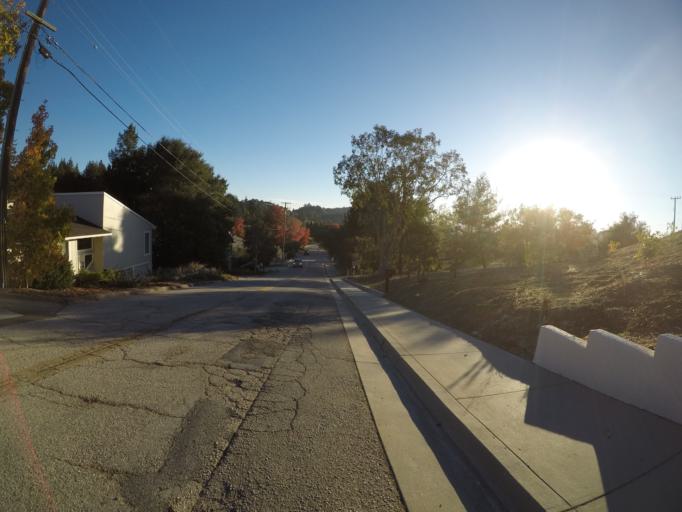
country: US
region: California
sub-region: Santa Cruz County
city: Scotts Valley
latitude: 37.0686
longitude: -121.9977
